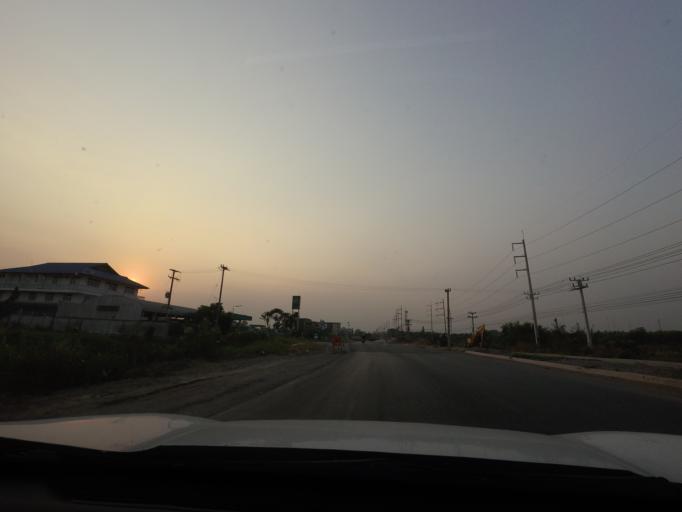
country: TH
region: Nakhon Nayok
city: Ongkharak
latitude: 14.1177
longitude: 101.0066
